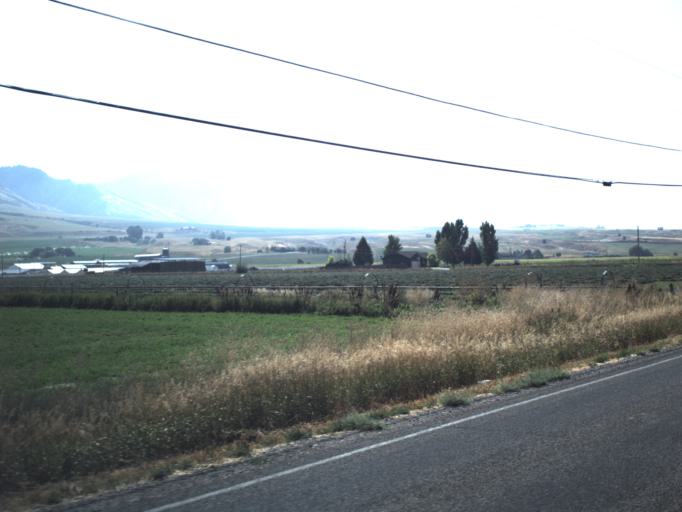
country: US
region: Utah
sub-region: Cache County
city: Hyrum
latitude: 41.6182
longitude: -111.8327
